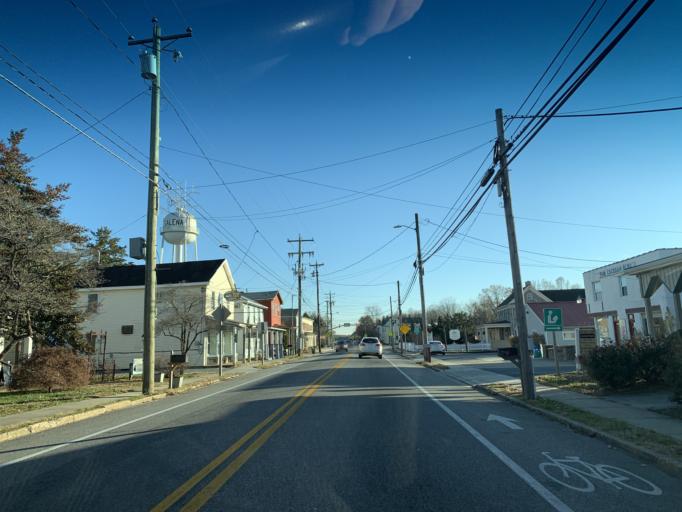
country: US
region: Delaware
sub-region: New Castle County
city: Townsend
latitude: 39.3421
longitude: -75.8791
